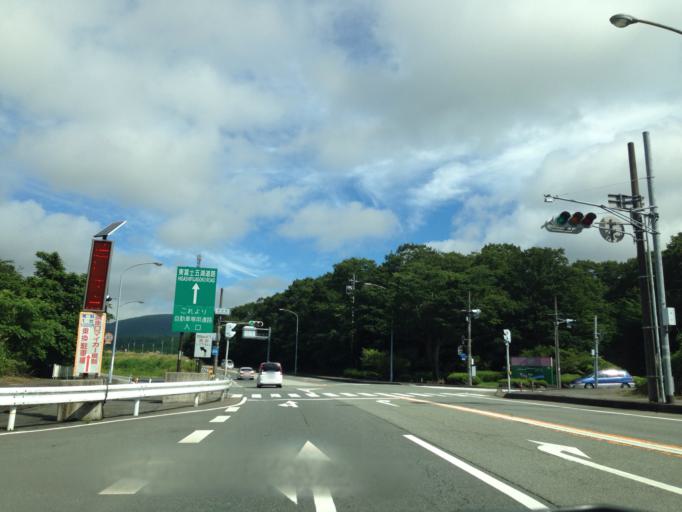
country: JP
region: Shizuoka
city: Gotemba
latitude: 35.3531
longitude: 138.8747
